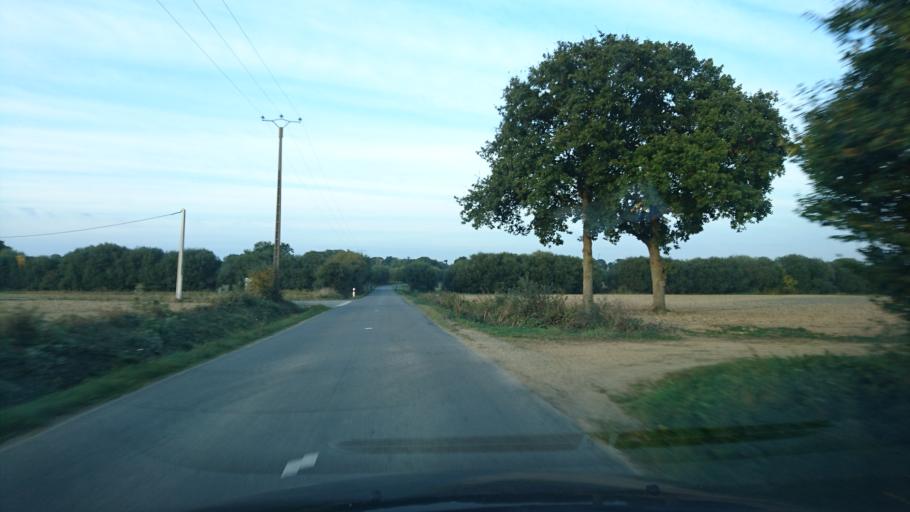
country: FR
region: Brittany
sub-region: Departement d'Ille-et-Vilaine
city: Sixt-sur-Aff
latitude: 47.8014
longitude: -2.0599
